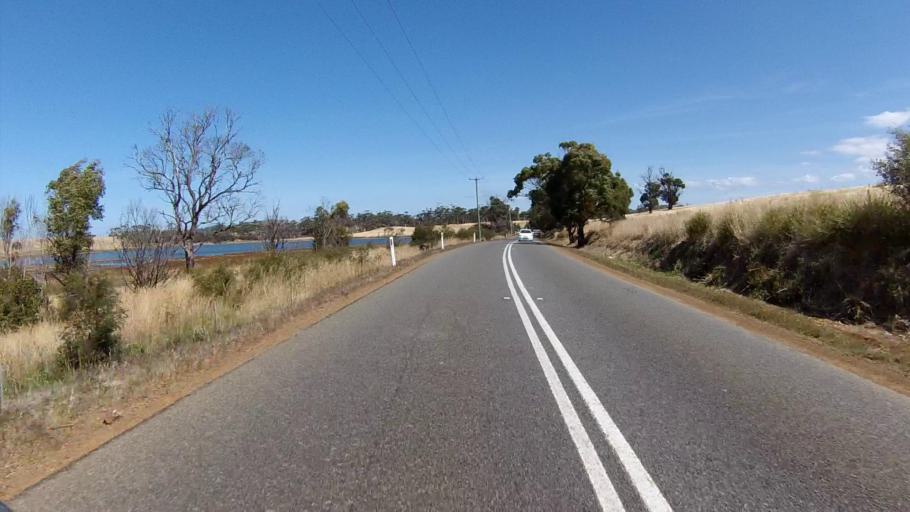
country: AU
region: Tasmania
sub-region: Sorell
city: Sorell
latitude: -42.2771
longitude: 148.0038
